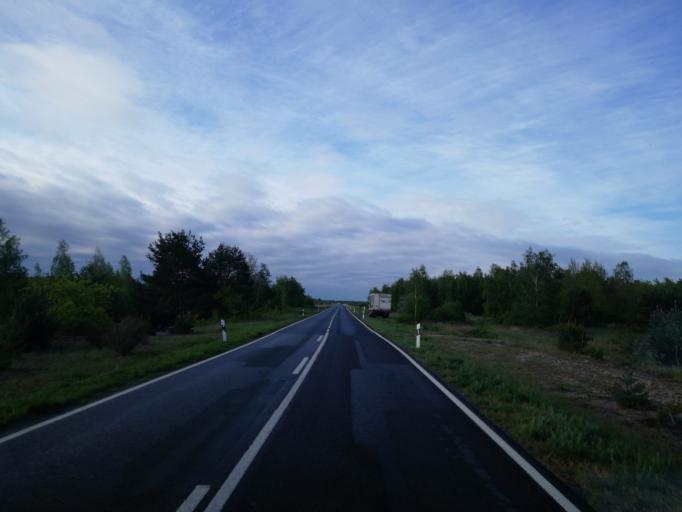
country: DE
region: Brandenburg
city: Lauchhammer
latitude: 51.5610
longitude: 13.7758
